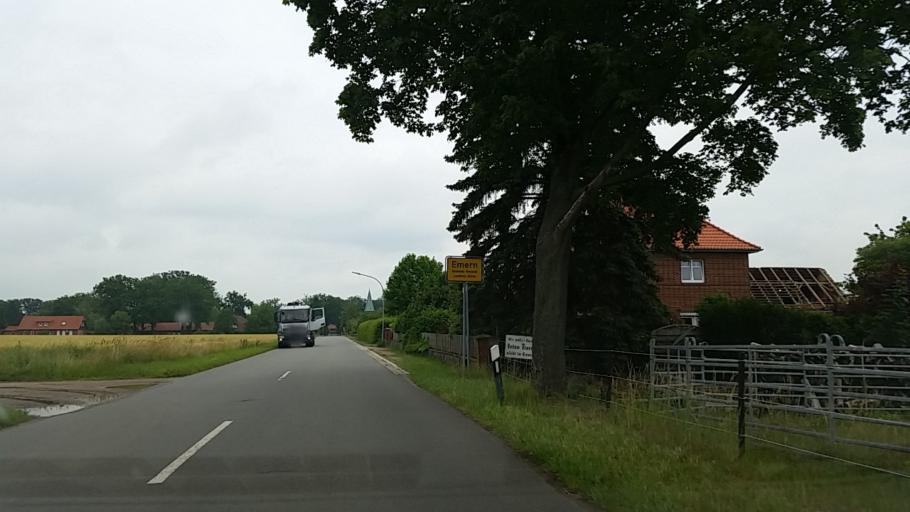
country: DE
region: Lower Saxony
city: Wieren
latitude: 52.9061
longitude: 10.6651
